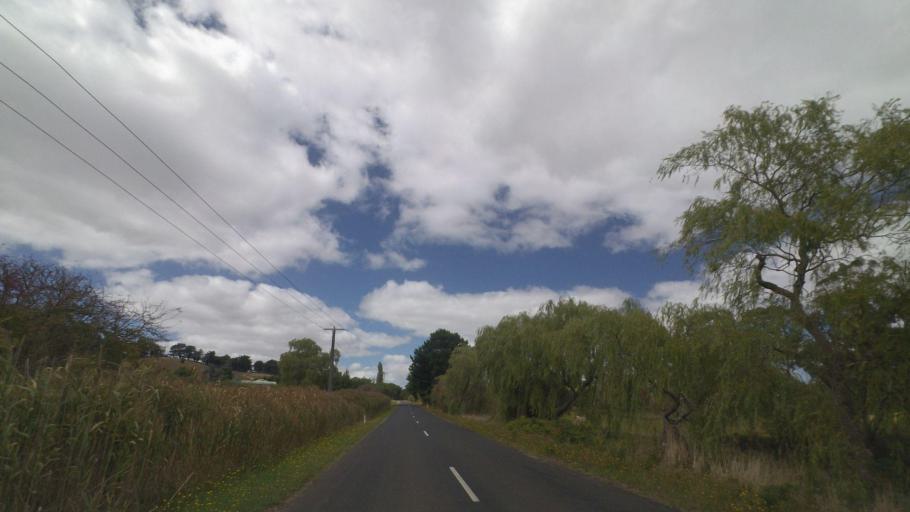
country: AU
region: Victoria
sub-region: Cardinia
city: Bunyip
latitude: -38.3494
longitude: 145.7000
